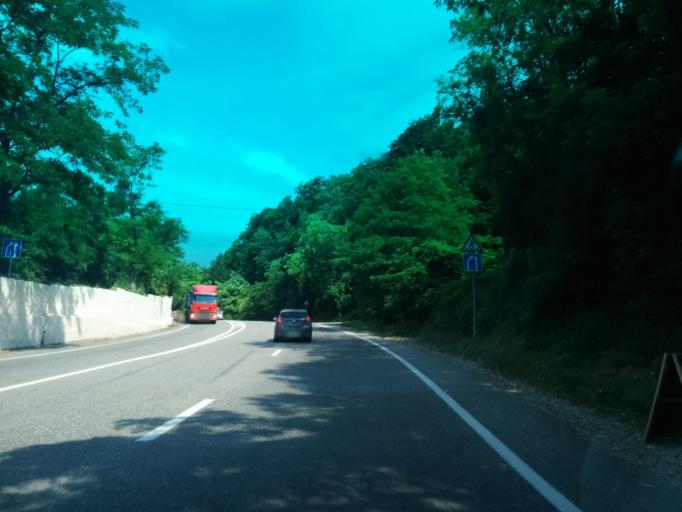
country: RU
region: Krasnodarskiy
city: Nebug
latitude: 44.1658
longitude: 38.9921
